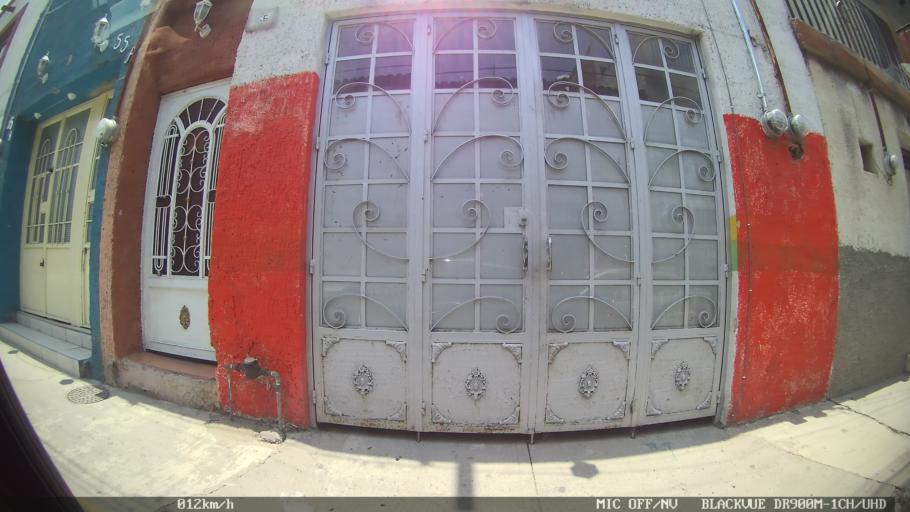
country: MX
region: Jalisco
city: Tonala
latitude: 20.6244
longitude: -103.2396
